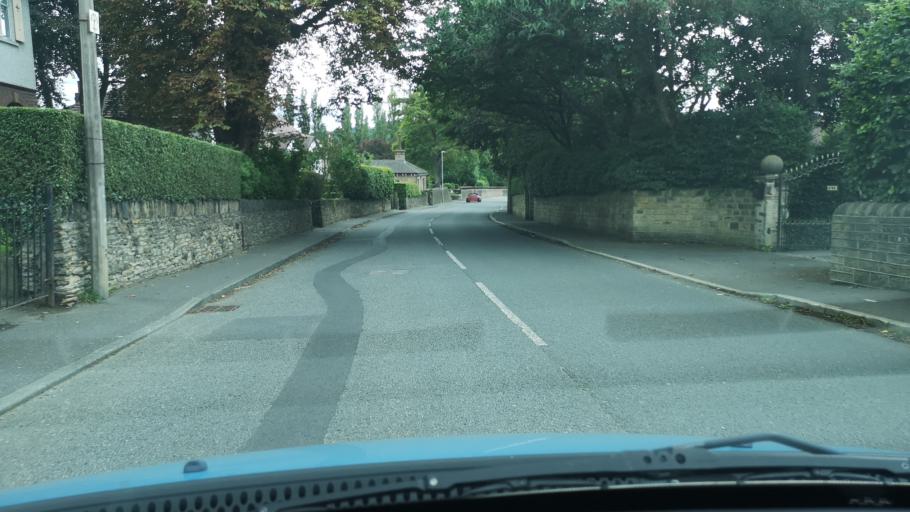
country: GB
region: England
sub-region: Kirklees
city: Mirfield
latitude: 53.6773
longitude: -1.6788
